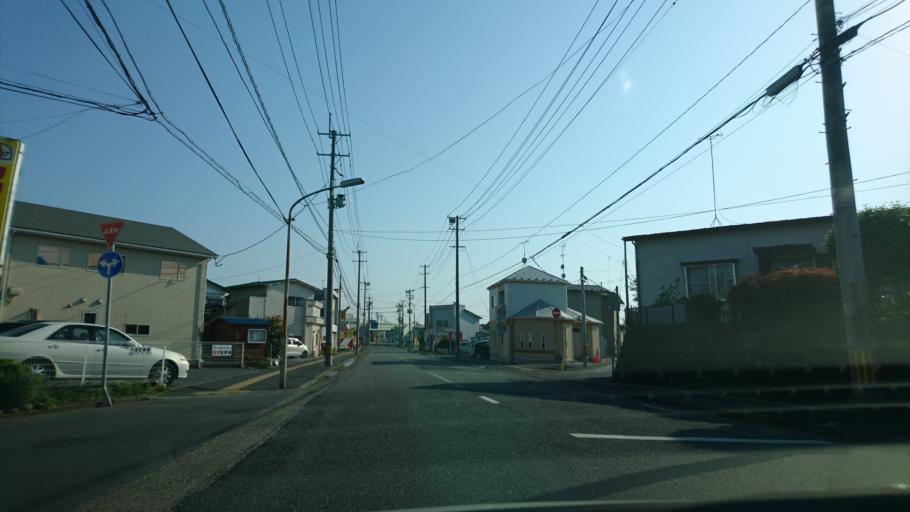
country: JP
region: Iwate
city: Ichinoseki
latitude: 38.9325
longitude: 141.1239
